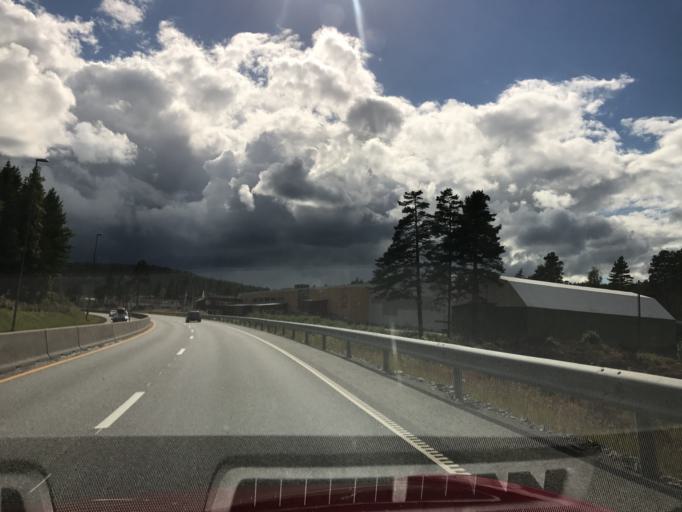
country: NO
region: Aust-Agder
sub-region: Gjerstad
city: Gjerstad
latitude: 58.8267
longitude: 9.0795
